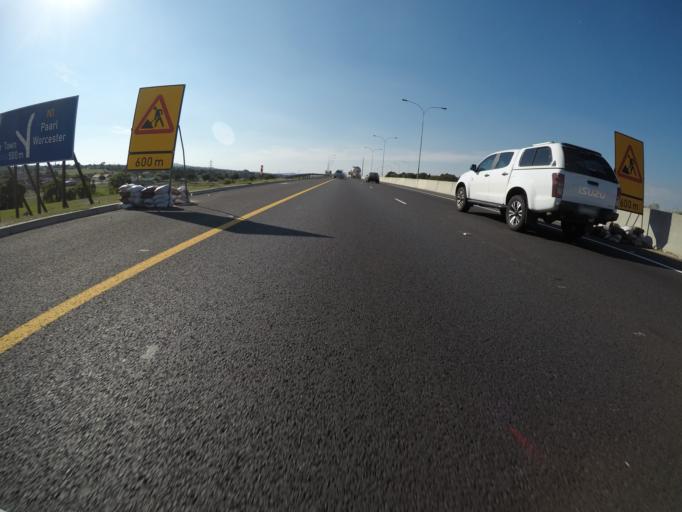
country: ZA
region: Western Cape
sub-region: City of Cape Town
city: Kraaifontein
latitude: -33.8808
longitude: 18.6735
